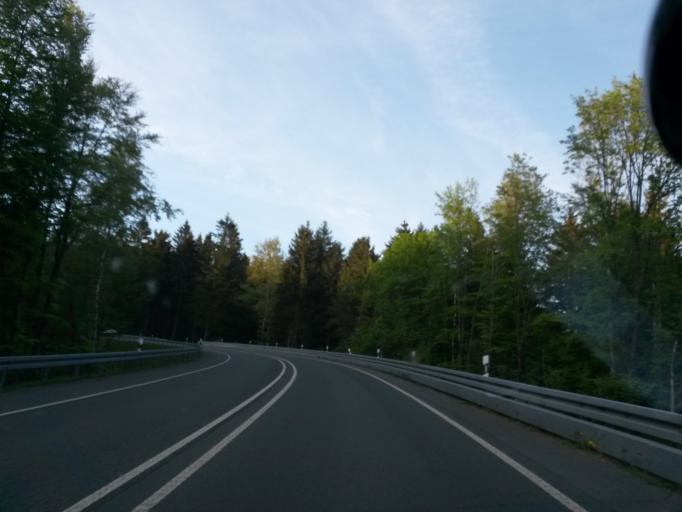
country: DE
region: North Rhine-Westphalia
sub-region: Regierungsbezirk Arnsberg
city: Herscheid
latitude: 51.1278
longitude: 7.7514
